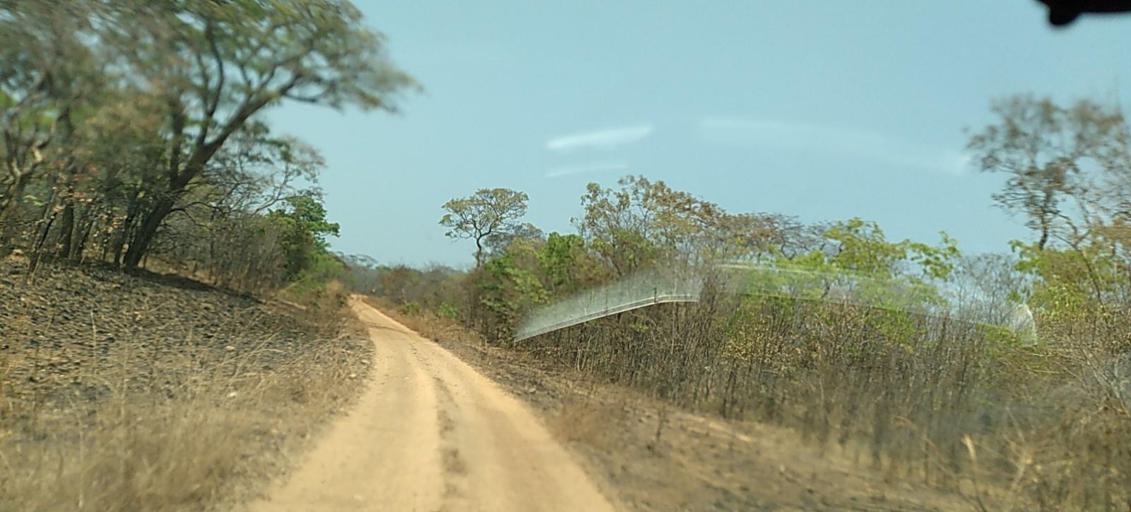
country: ZM
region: Central
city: Mumbwa
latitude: -14.4032
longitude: 26.4885
